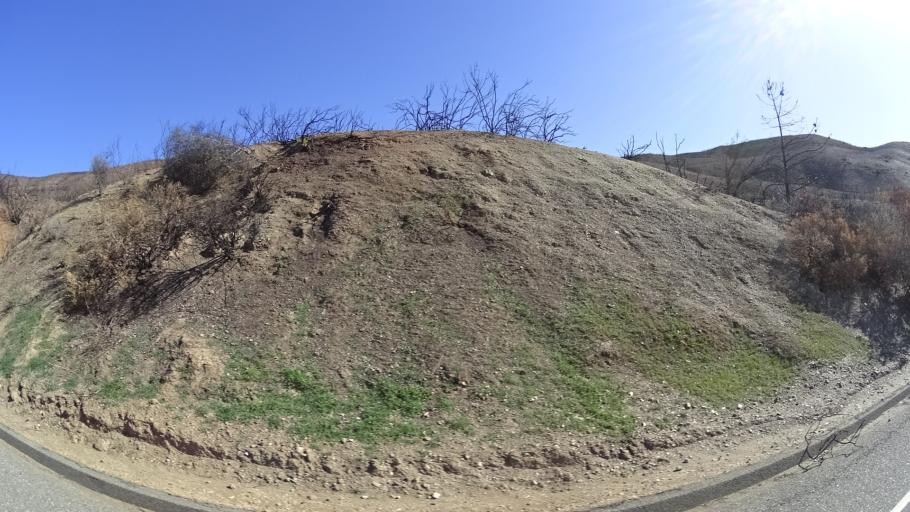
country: US
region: California
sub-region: Tehama County
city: Rancho Tehama Reserve
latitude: 39.6577
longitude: -122.6229
